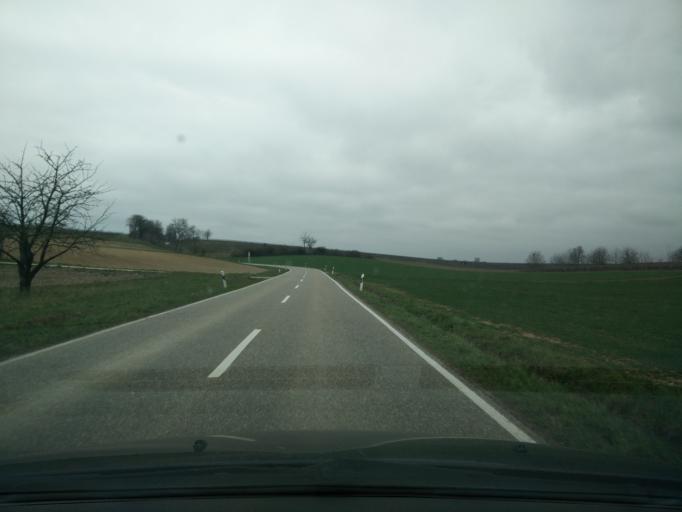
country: DE
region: Rheinland-Pfalz
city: Billigheim-Ingenheim
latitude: 49.1237
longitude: 8.0905
